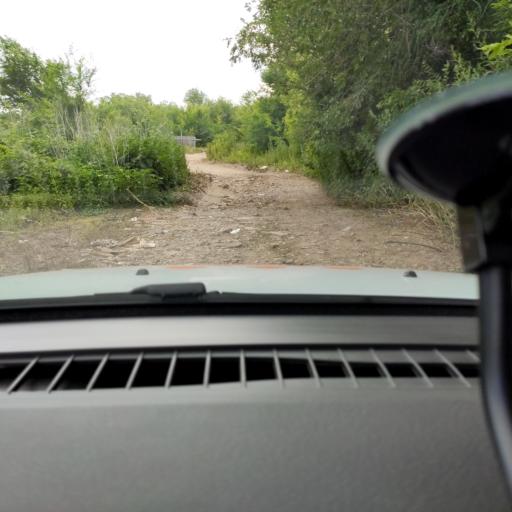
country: RU
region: Samara
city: Samara
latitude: 53.1783
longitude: 50.2161
